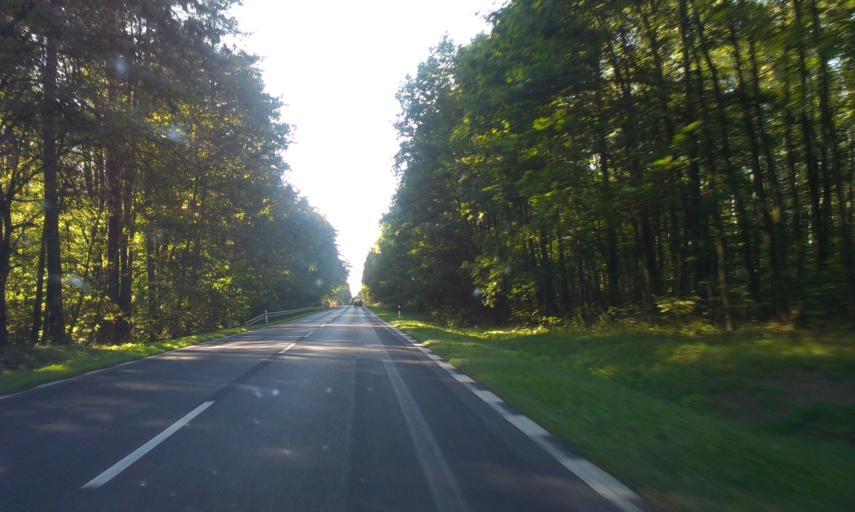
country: PL
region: Kujawsko-Pomorskie
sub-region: Powiat swiecki
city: Swiekatowo
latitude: 53.4862
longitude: 18.1207
